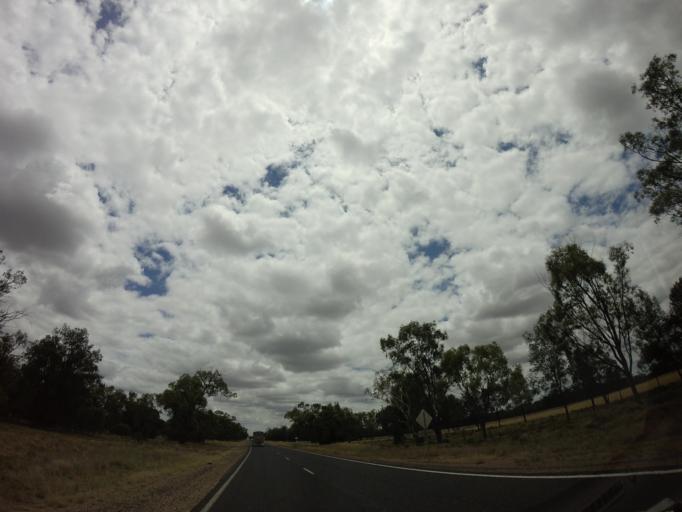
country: AU
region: Queensland
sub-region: Goondiwindi
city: Goondiwindi
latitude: -28.4479
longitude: 150.2992
